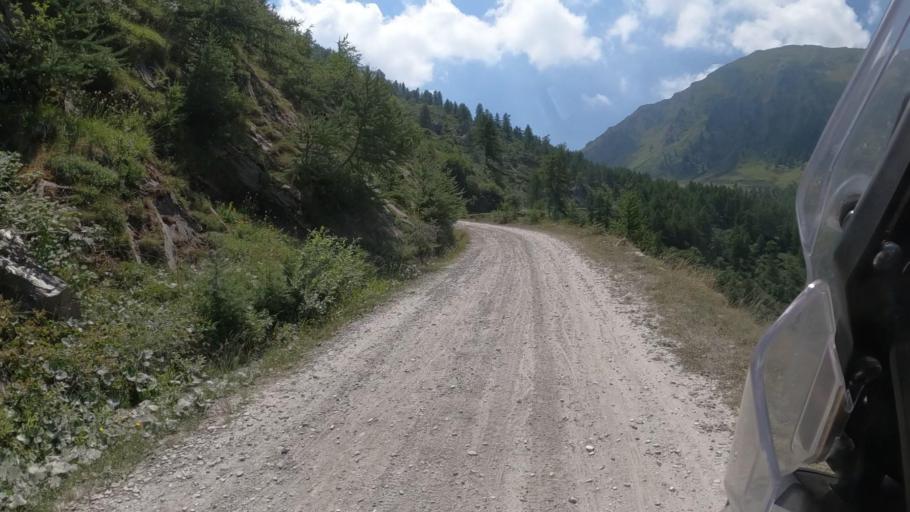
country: IT
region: Piedmont
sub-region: Provincia di Torino
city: Meana di Susa
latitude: 45.0862
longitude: 7.0637
